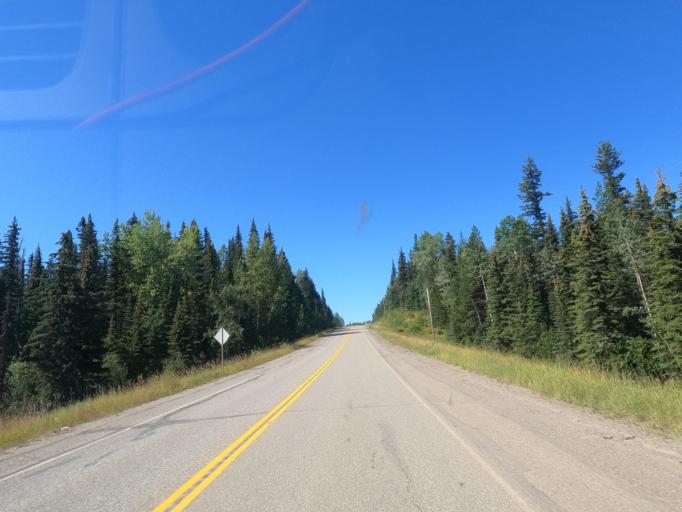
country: CA
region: British Columbia
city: Quesnel
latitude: 53.0332
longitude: -122.2667
